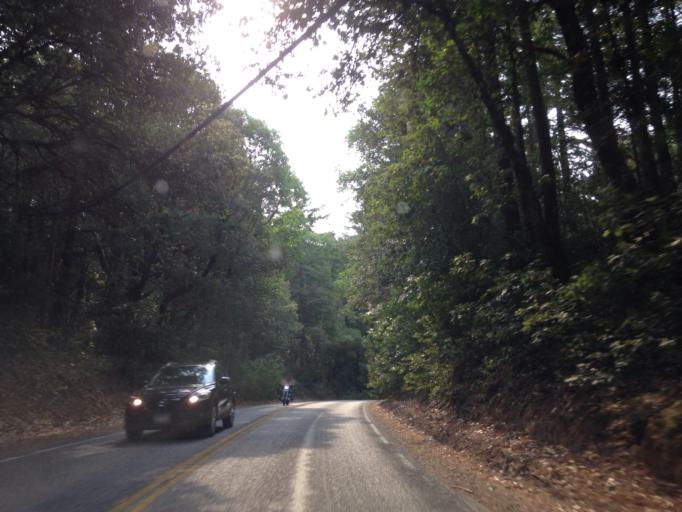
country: US
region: California
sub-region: San Mateo County
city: Emerald Lake Hills
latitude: 37.4346
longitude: -122.3181
